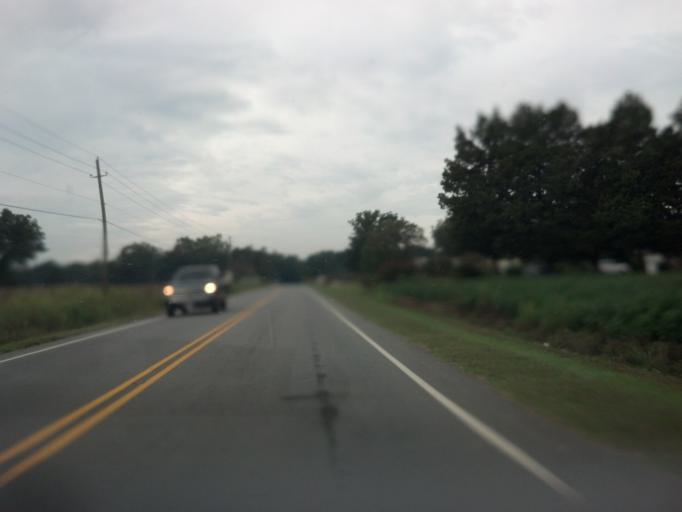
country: US
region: North Carolina
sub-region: Pitt County
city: Ayden
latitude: 35.4754
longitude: -77.4648
